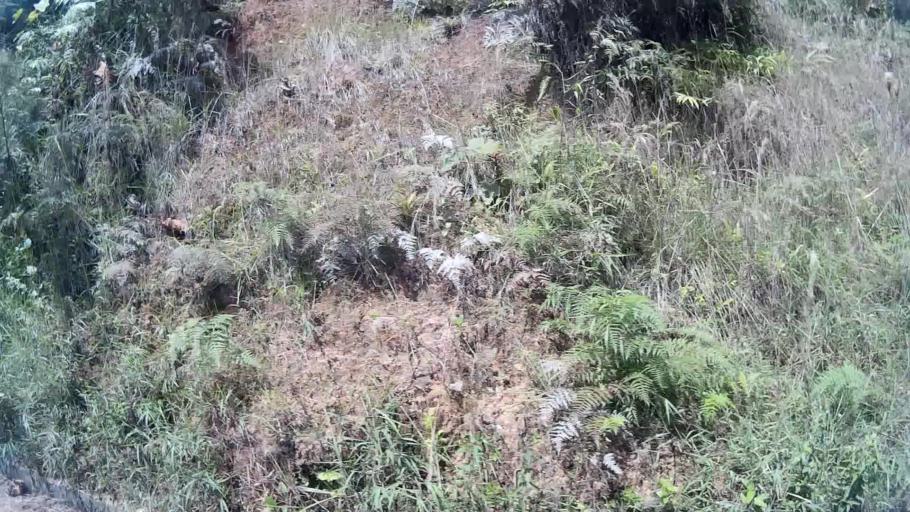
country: CO
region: Caldas
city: Belalcazar
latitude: 4.9534
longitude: -75.8318
